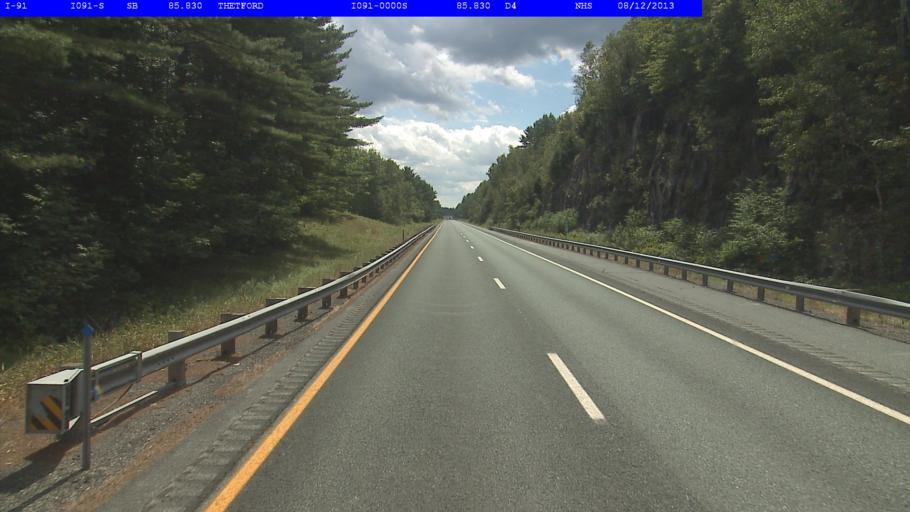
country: US
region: New Hampshire
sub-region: Grafton County
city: Lyme
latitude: 43.8345
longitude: -72.2058
